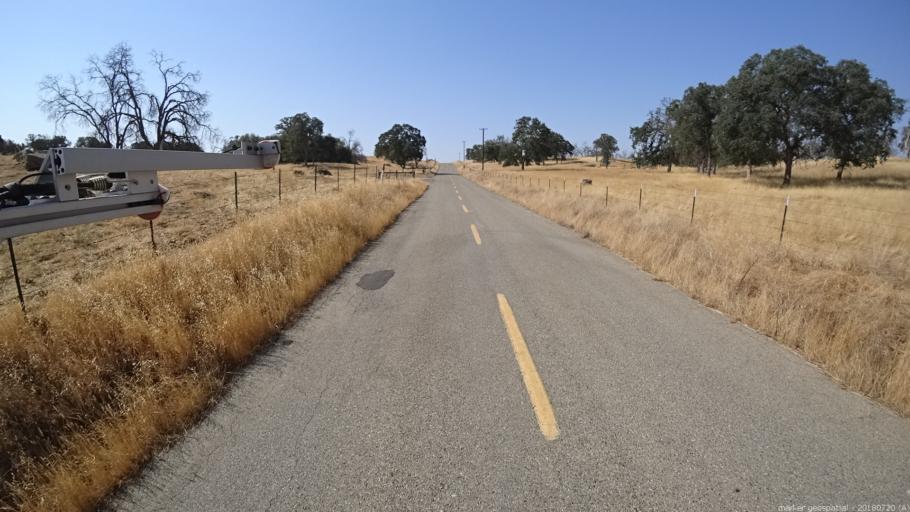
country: US
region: California
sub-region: Madera County
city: Yosemite Lakes
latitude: 37.2462
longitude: -119.9250
